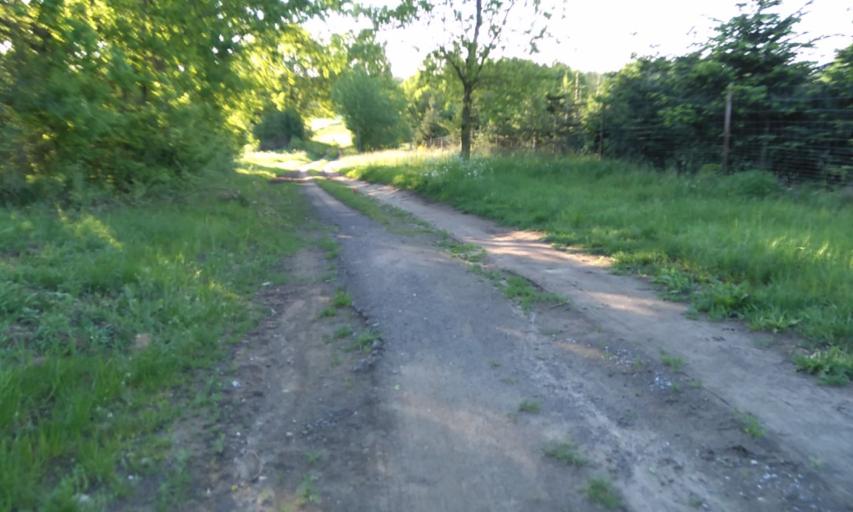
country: DE
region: Lower Saxony
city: Bliedersdorf
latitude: 53.4913
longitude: 9.5673
